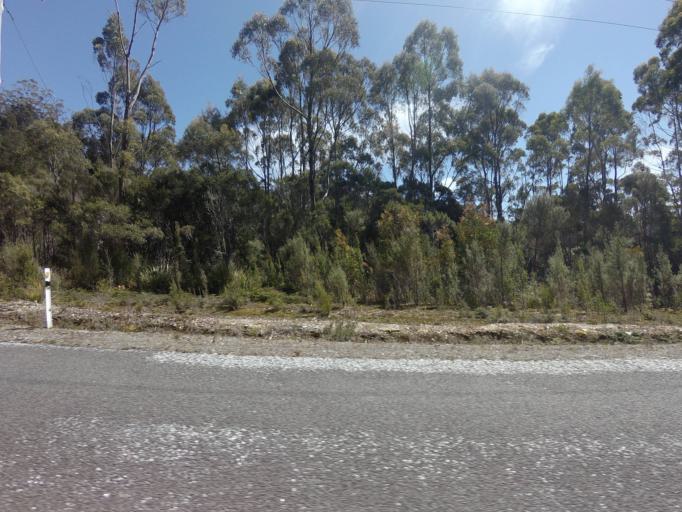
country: AU
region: Tasmania
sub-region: West Coast
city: Queenstown
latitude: -42.7554
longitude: 145.9945
